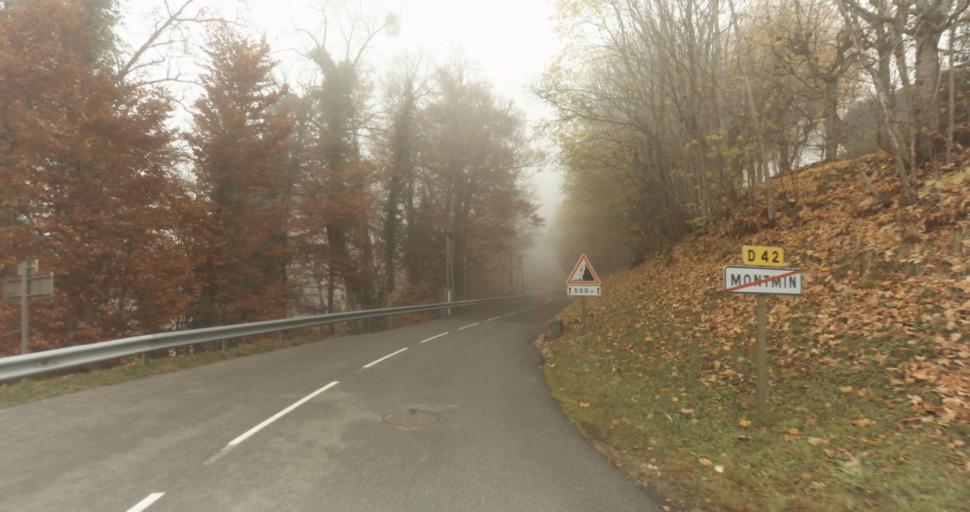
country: FR
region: Rhone-Alpes
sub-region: Departement de la Haute-Savoie
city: Doussard
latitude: 45.8053
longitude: 6.2633
